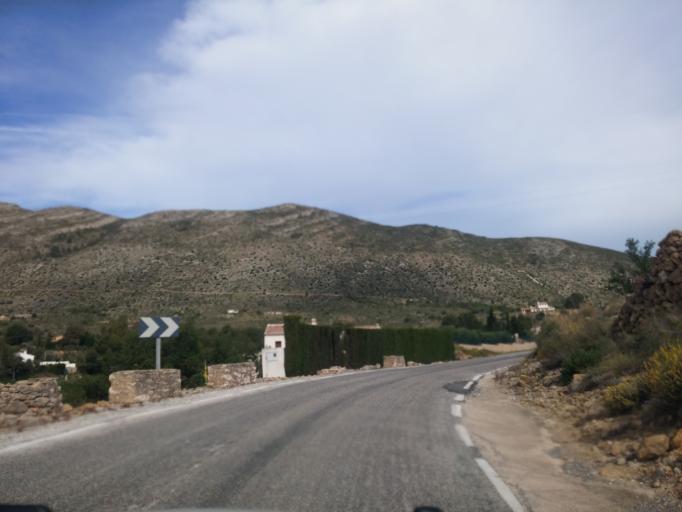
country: ES
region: Valencia
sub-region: Provincia de Alicante
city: Benissa
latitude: 38.7065
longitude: 0.0202
